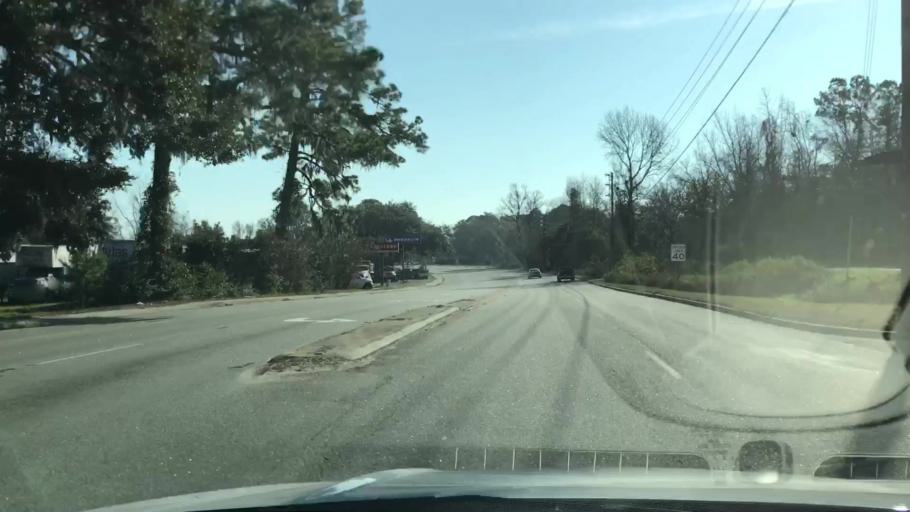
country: US
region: South Carolina
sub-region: Beaufort County
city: Burton
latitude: 32.4400
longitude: -80.7154
